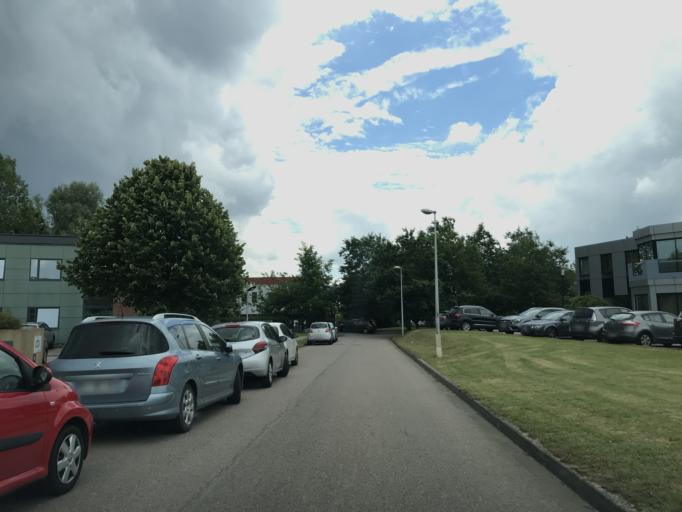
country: FR
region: Haute-Normandie
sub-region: Departement de la Seine-Maritime
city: Mont-Saint-Aignan
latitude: 49.4749
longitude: 1.0983
